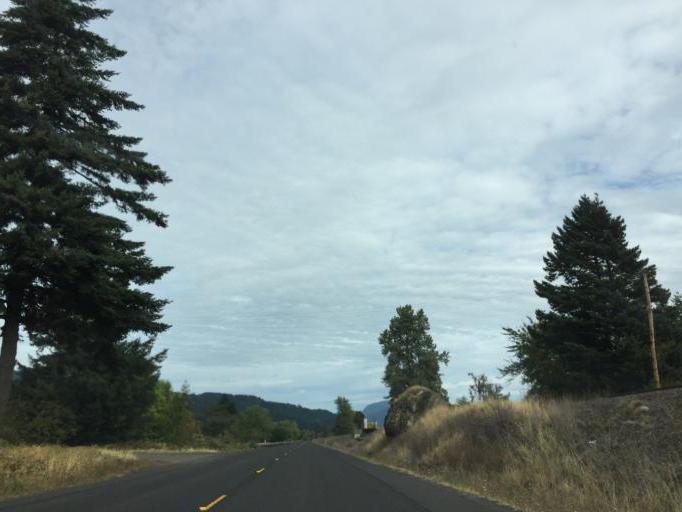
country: US
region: Oregon
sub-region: Hood River County
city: Cascade Locks
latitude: 45.6841
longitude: -121.8984
